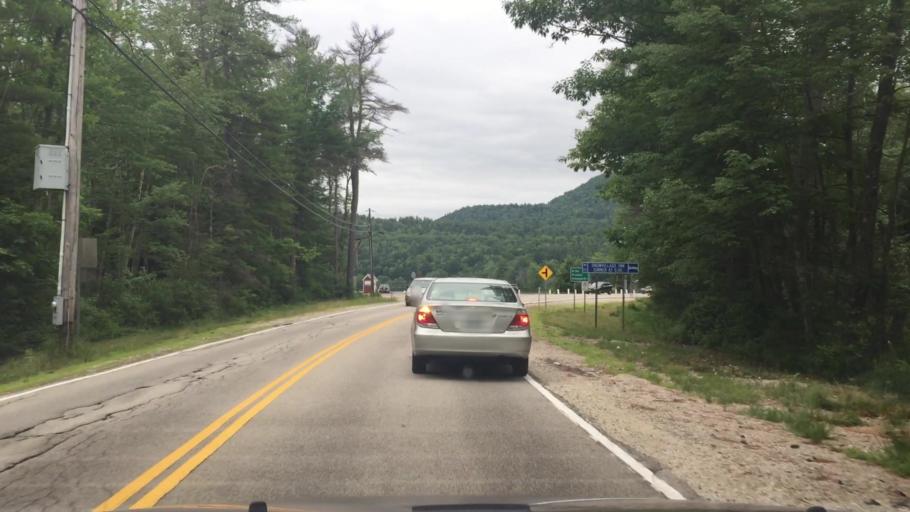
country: US
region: New Hampshire
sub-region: Carroll County
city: Madison
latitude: 43.9155
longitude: -71.0734
